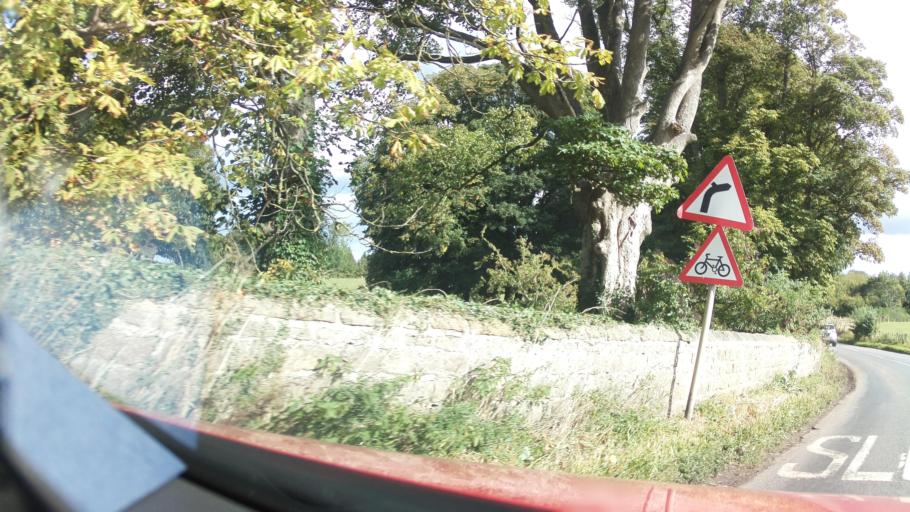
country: GB
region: England
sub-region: North Yorkshire
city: Leyburn
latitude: 54.2627
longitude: -1.7284
